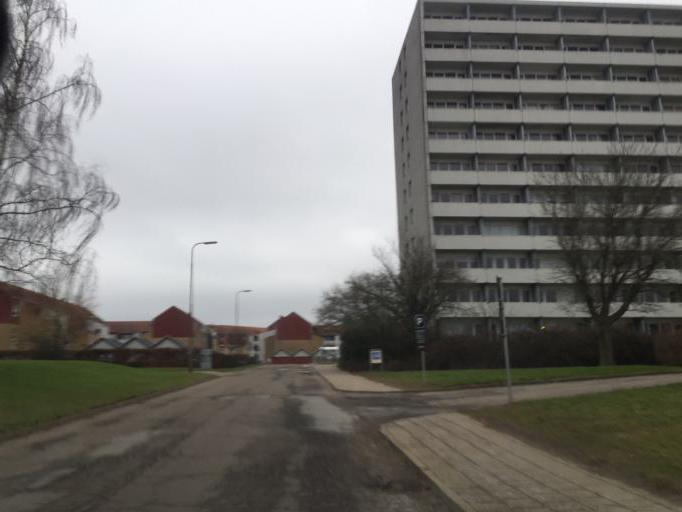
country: DK
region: South Denmark
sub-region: Haderslev Kommune
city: Haderslev
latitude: 55.2577
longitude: 9.4790
